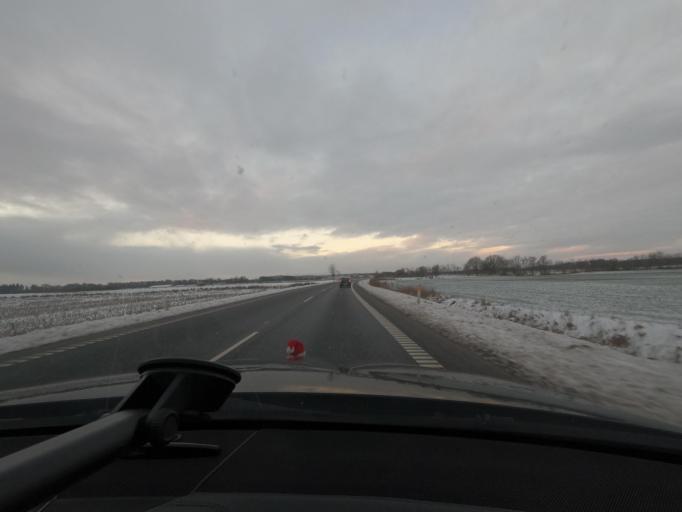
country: DK
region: South Denmark
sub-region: Aabenraa Kommune
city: Krusa
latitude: 54.8528
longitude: 9.4239
